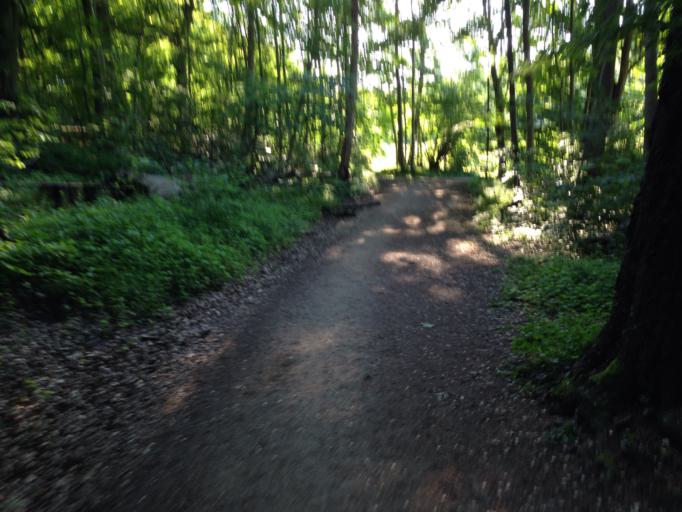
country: DK
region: Capital Region
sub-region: Gentofte Kommune
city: Charlottenlund
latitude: 55.7706
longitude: 12.5616
